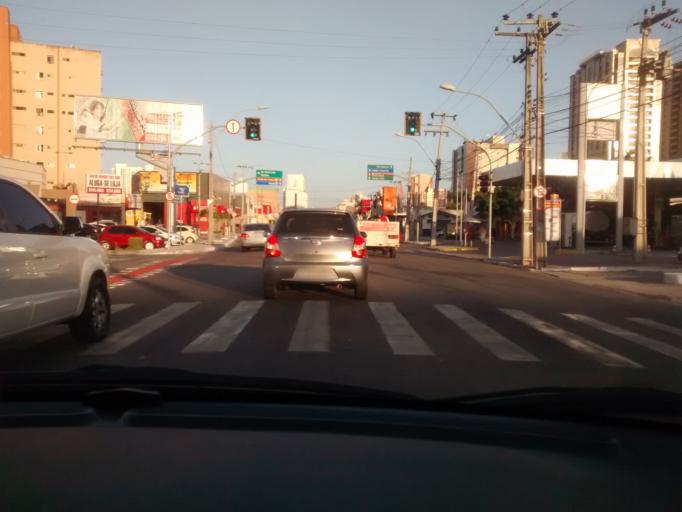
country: BR
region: Ceara
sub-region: Fortaleza
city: Fortaleza
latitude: -3.7392
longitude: -38.4893
